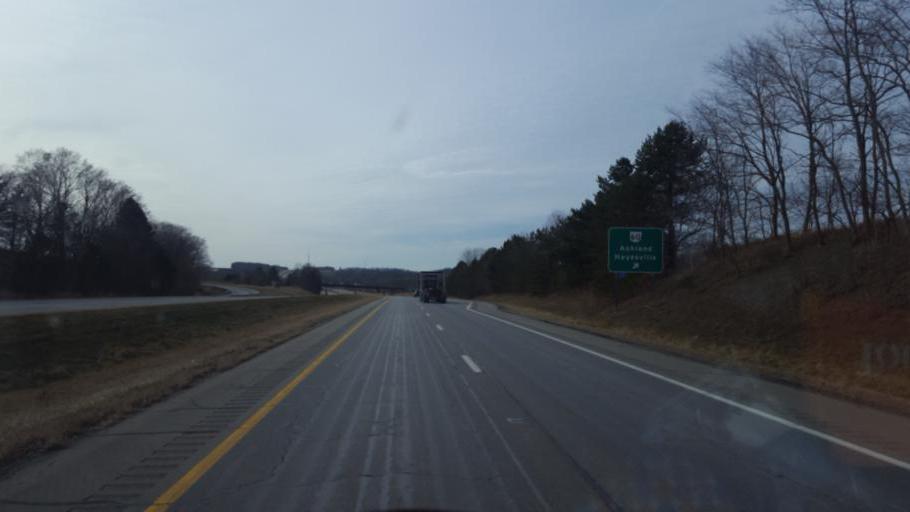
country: US
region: Ohio
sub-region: Ashland County
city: Ashland
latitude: 40.7853
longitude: -82.2570
